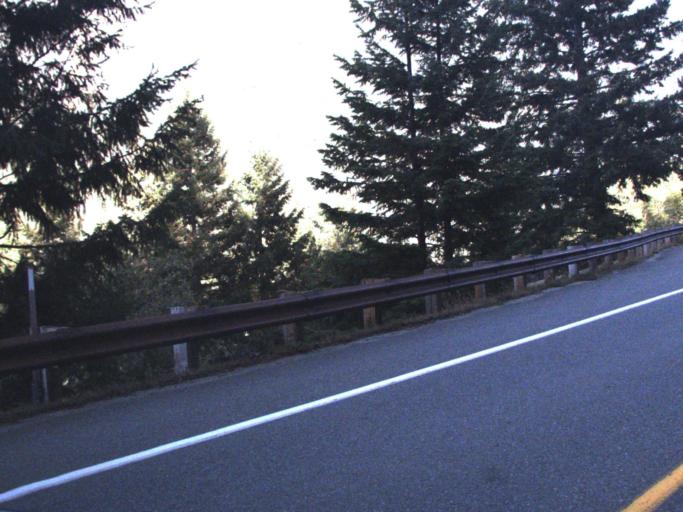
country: US
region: Washington
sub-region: Snohomish County
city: Darrington
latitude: 48.7278
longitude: -121.0396
